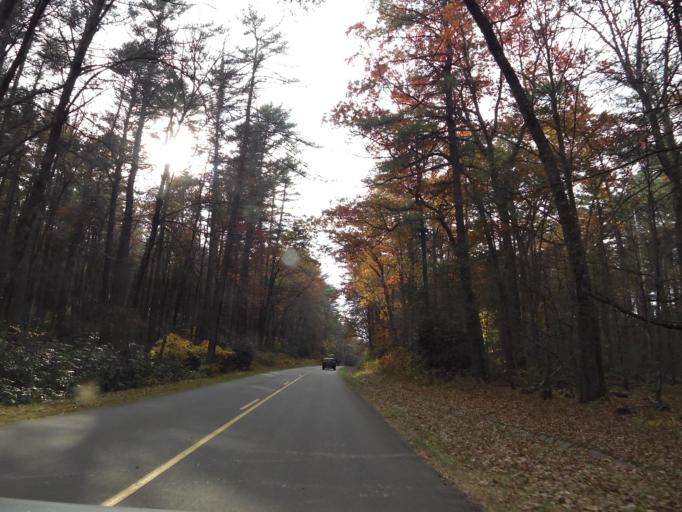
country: US
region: North Carolina
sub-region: Wilkes County
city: Mulberry
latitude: 36.3891
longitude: -81.2515
